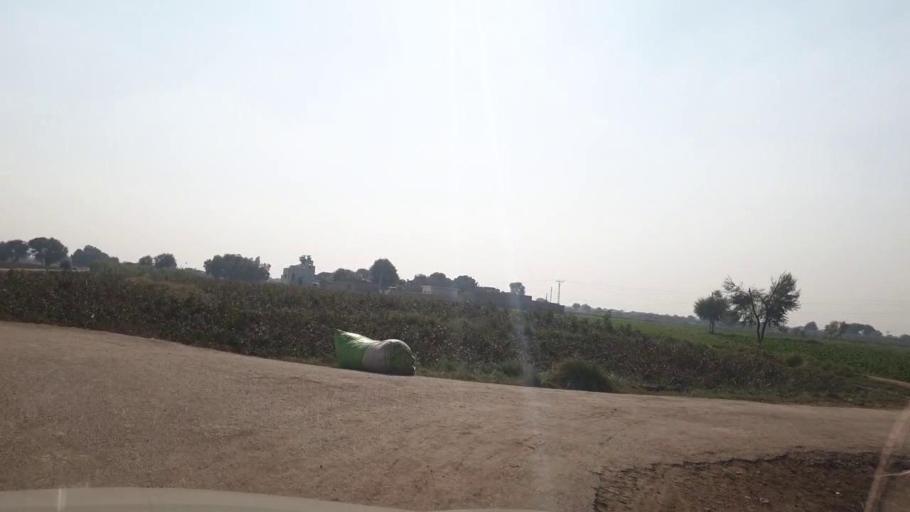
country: PK
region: Sindh
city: Bhan
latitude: 26.5312
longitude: 67.7434
